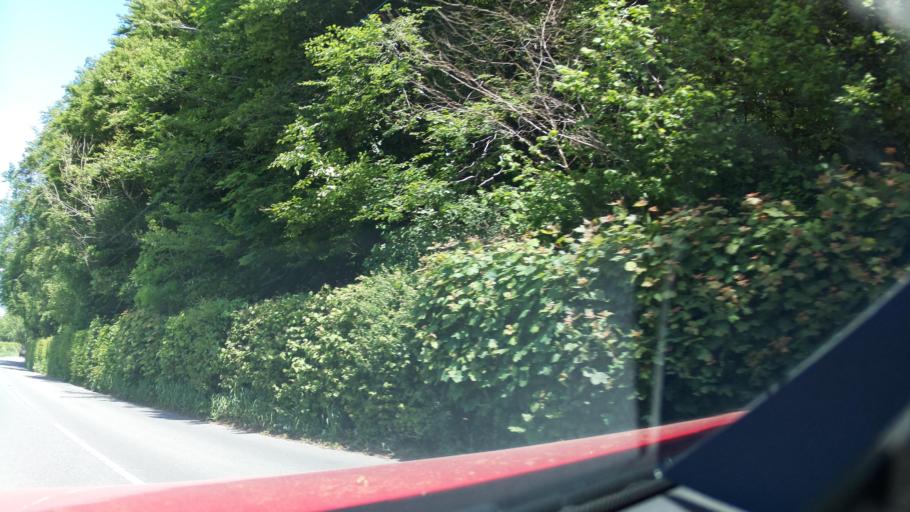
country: GB
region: Wales
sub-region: Monmouthshire
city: Llangwm
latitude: 51.7195
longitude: -2.7634
